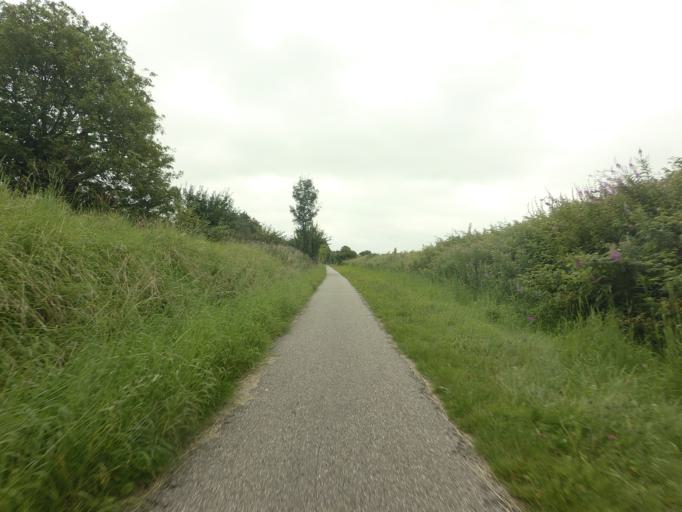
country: DK
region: Central Jutland
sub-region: Horsens Kommune
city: Braedstrup
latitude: 56.0238
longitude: 9.5615
